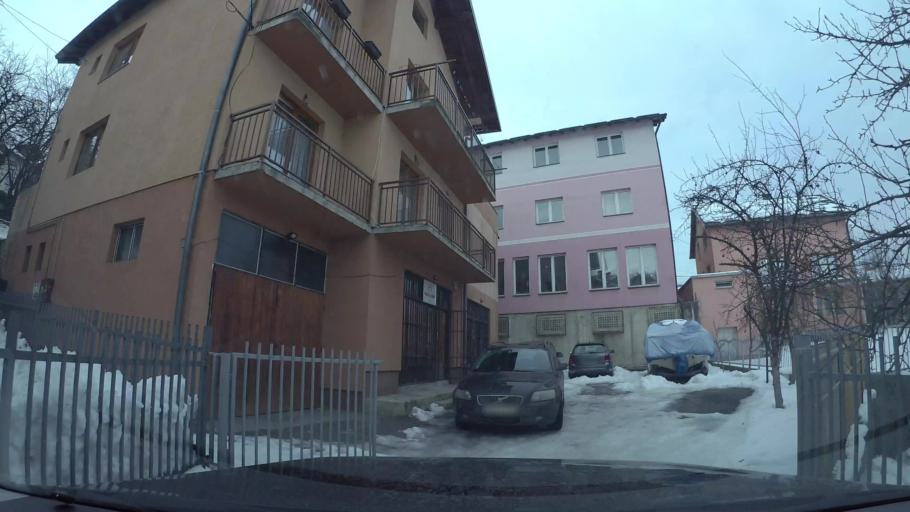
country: BA
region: Federation of Bosnia and Herzegovina
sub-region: Kanton Sarajevo
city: Sarajevo
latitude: 43.8609
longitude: 18.3584
